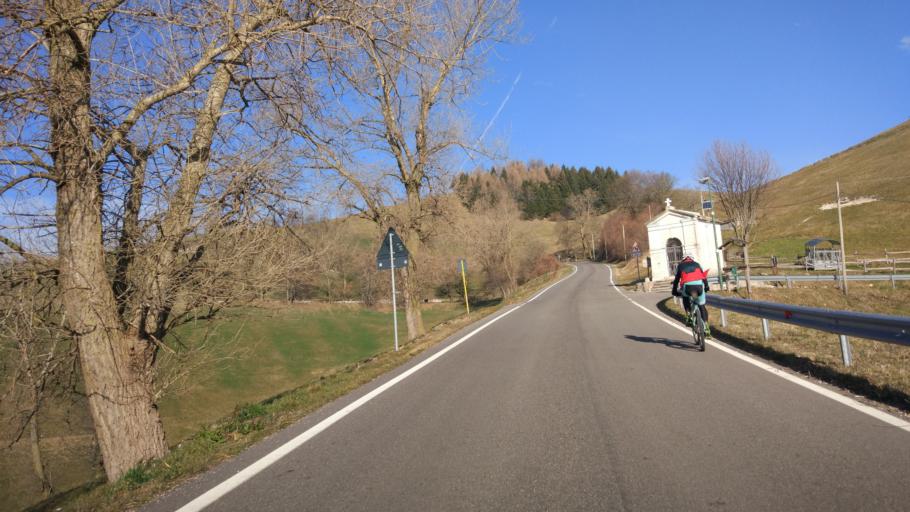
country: IT
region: Veneto
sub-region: Provincia di Verona
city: Selva di Progno
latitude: 45.6210
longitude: 11.1666
